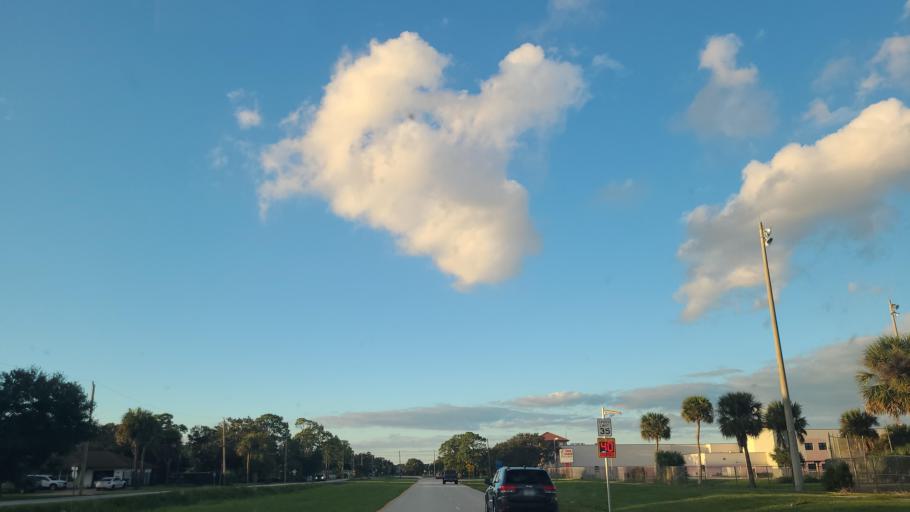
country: US
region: Florida
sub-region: Indian River County
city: Vero Beach South
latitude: 27.6276
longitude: -80.4057
